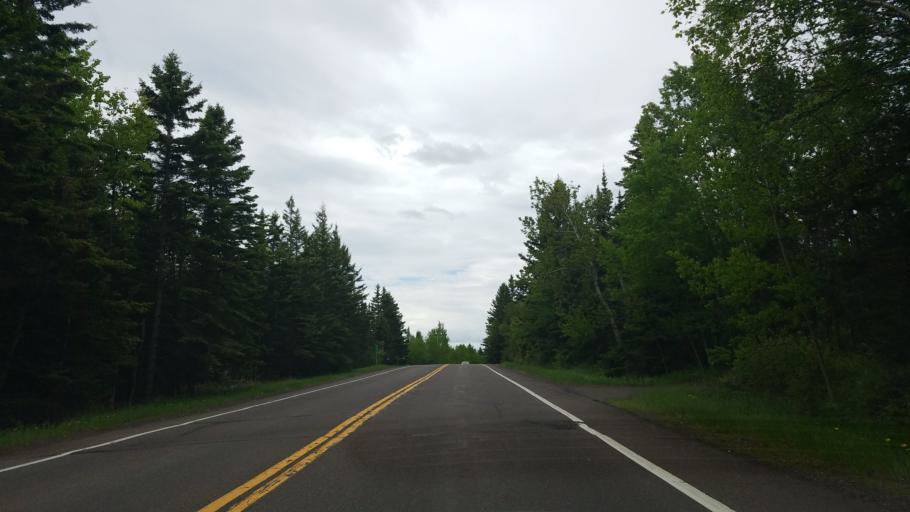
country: US
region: Minnesota
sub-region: Lake County
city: Two Harbors
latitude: 47.0536
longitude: -91.6215
